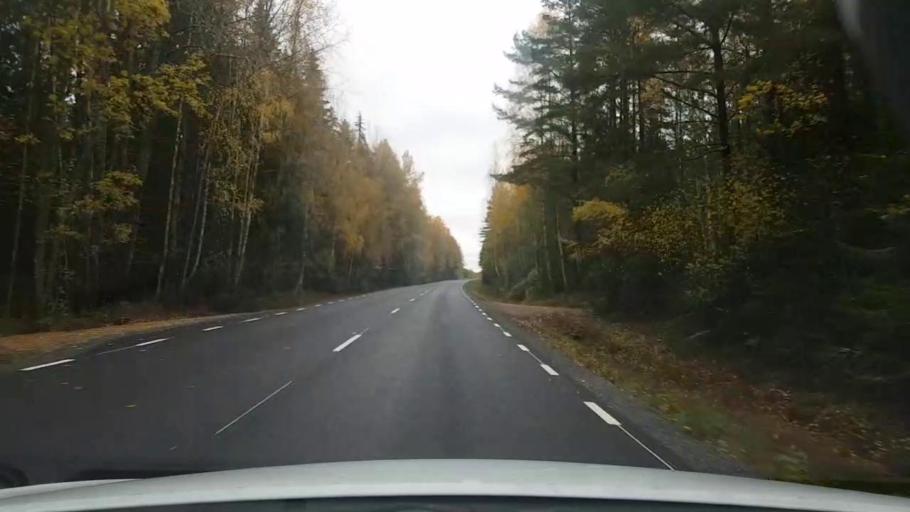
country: SE
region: OErebro
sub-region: Laxa Kommun
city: Laxa
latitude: 58.8041
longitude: 14.5430
